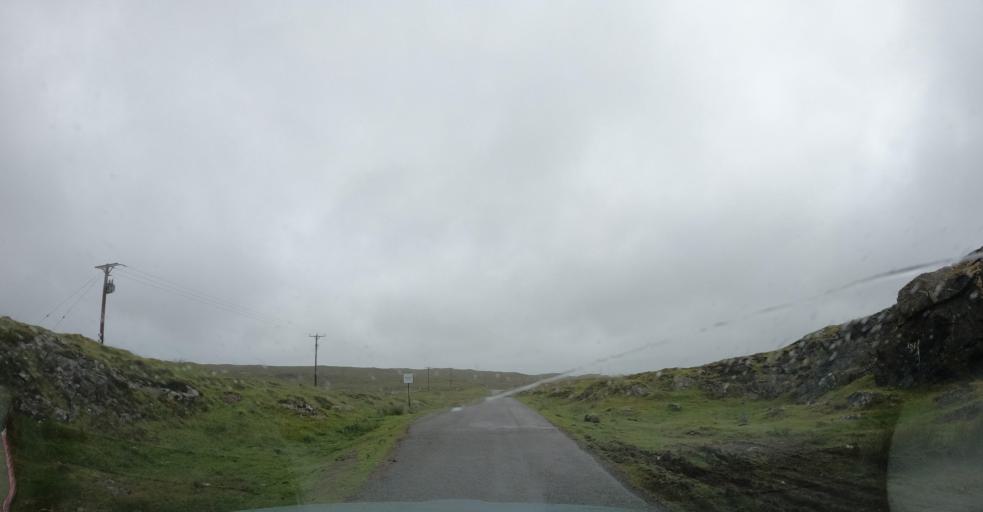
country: GB
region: Scotland
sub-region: Eilean Siar
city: Benbecula
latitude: 57.4949
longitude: -7.2337
